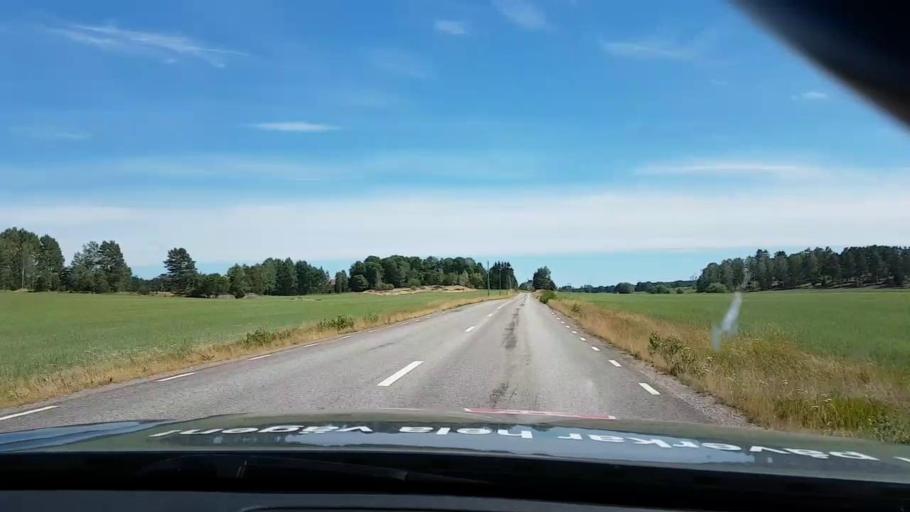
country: SE
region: Kalmar
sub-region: Vasterviks Kommun
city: Forserum
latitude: 57.9388
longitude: 16.5001
